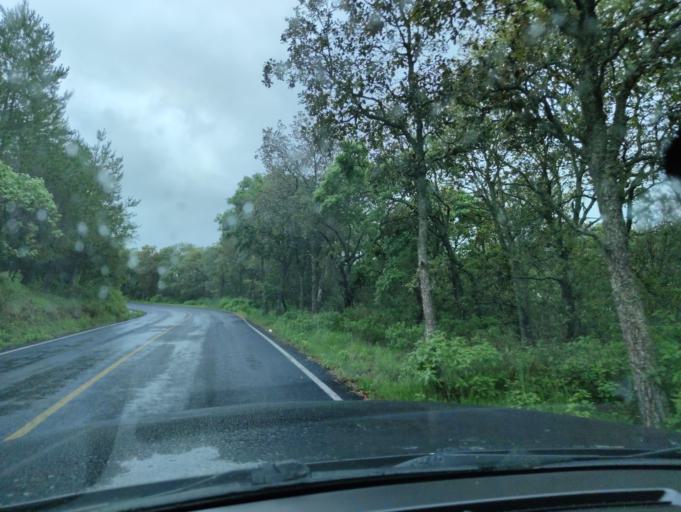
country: MX
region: Mexico
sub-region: Morelos
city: San Marcos Tlazalpan
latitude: 19.8755
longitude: -99.6600
